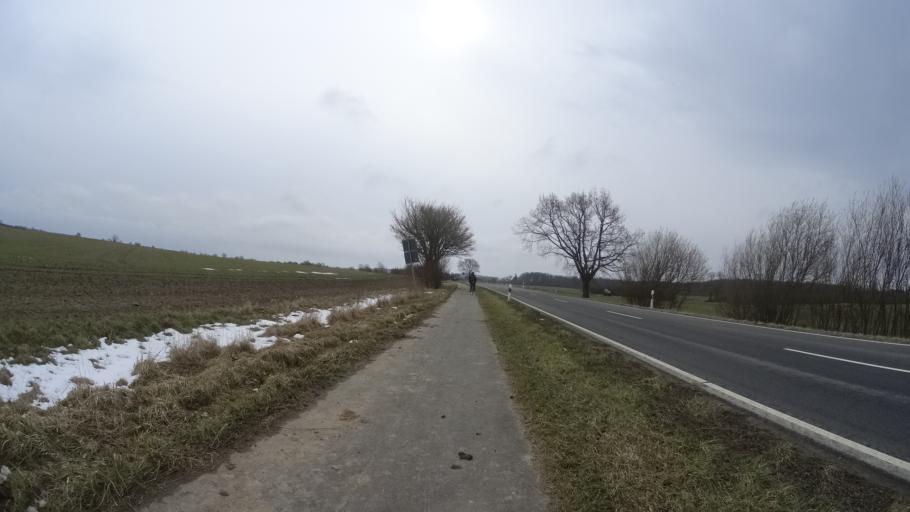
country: DE
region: Schleswig-Holstein
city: Hohenfelde
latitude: 54.3659
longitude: 10.5127
